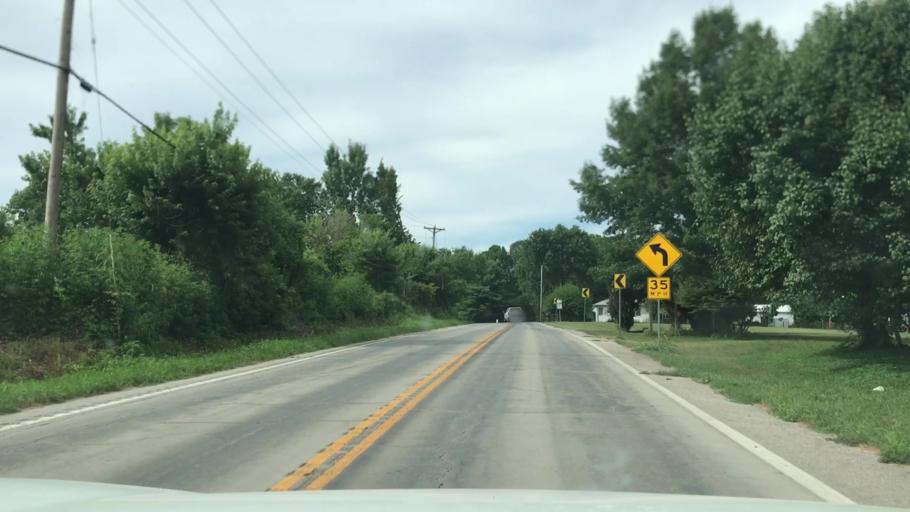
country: US
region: Missouri
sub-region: Saint Charles County
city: Weldon Spring
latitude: 38.6478
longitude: -90.7754
